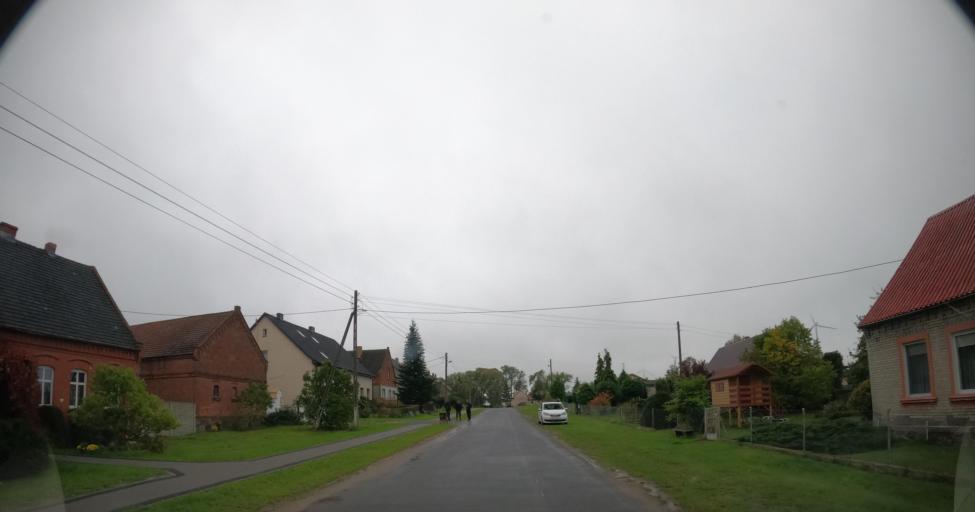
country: PL
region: West Pomeranian Voivodeship
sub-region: Powiat pyrzycki
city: Kozielice
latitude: 53.0730
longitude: 14.7875
